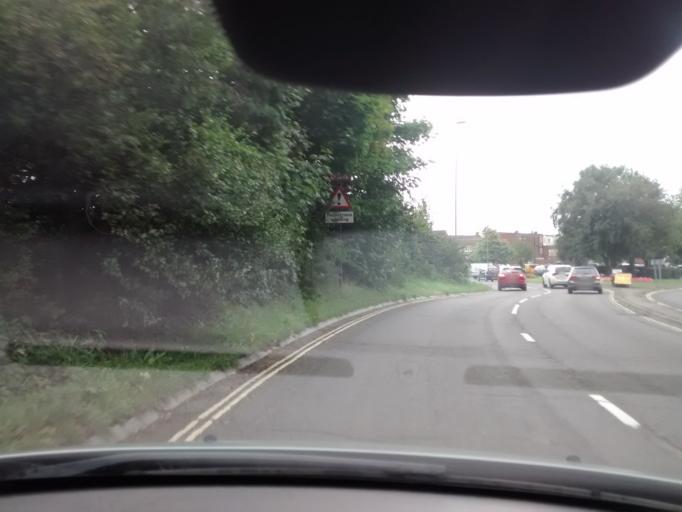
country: GB
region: England
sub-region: Hampshire
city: Ringwood
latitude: 50.8486
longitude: -1.7906
